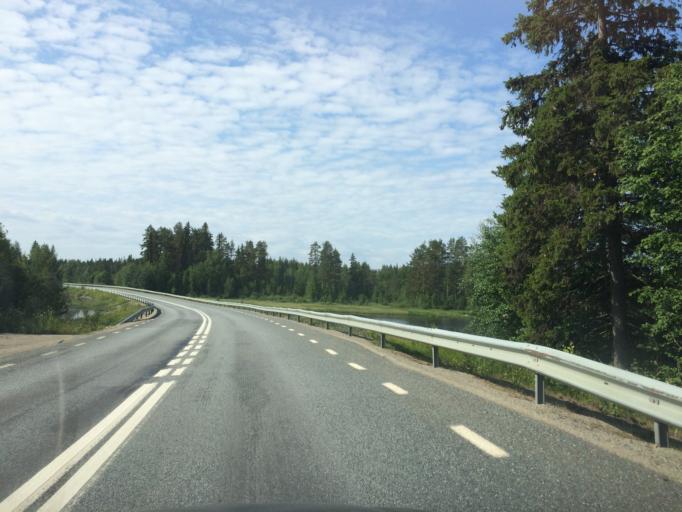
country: SE
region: Vaesternorrland
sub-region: Kramfors Kommun
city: Bollstabruk
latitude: 63.1679
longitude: 17.7925
